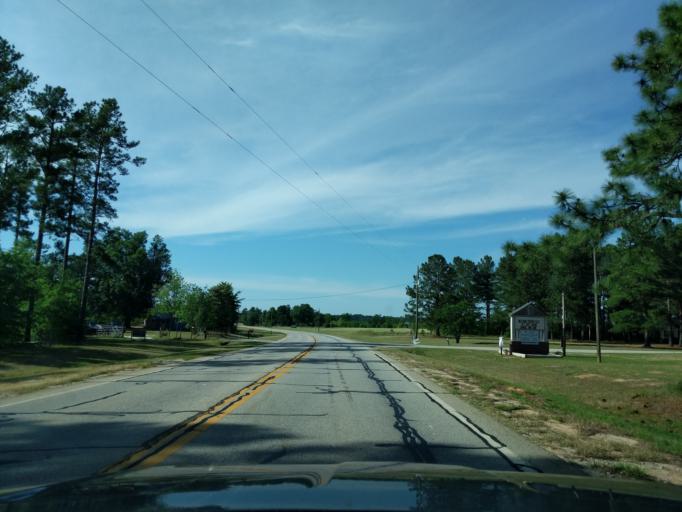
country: US
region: Georgia
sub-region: Jefferson County
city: Wrens
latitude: 33.2620
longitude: -82.3845
